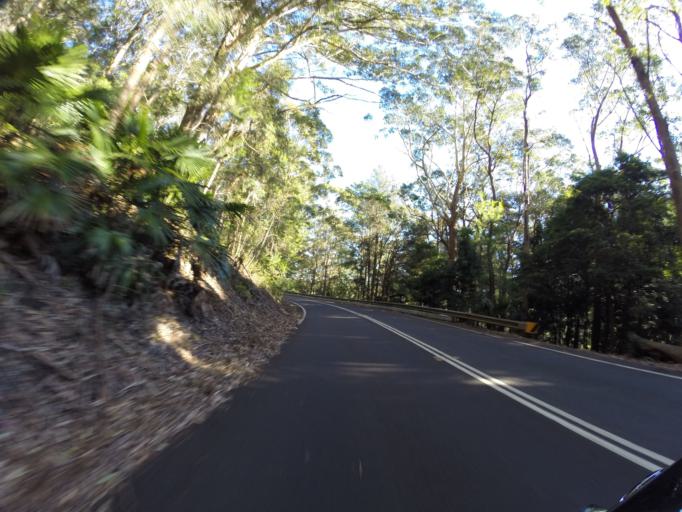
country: AU
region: New South Wales
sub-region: Wollongong
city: Helensburgh
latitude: -34.1987
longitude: 151.0103
